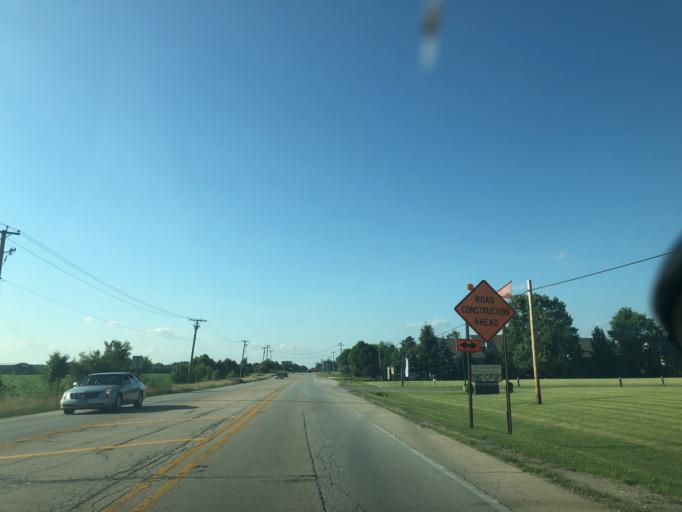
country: US
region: Illinois
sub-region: Will County
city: Homer Glen
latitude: 41.5924
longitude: -87.8912
